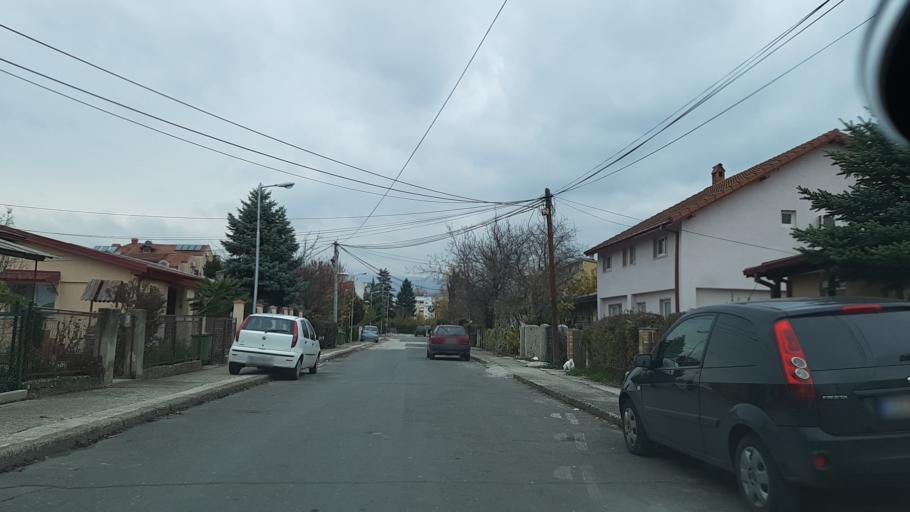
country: MK
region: Kisela Voda
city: Usje
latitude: 41.9762
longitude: 21.4709
